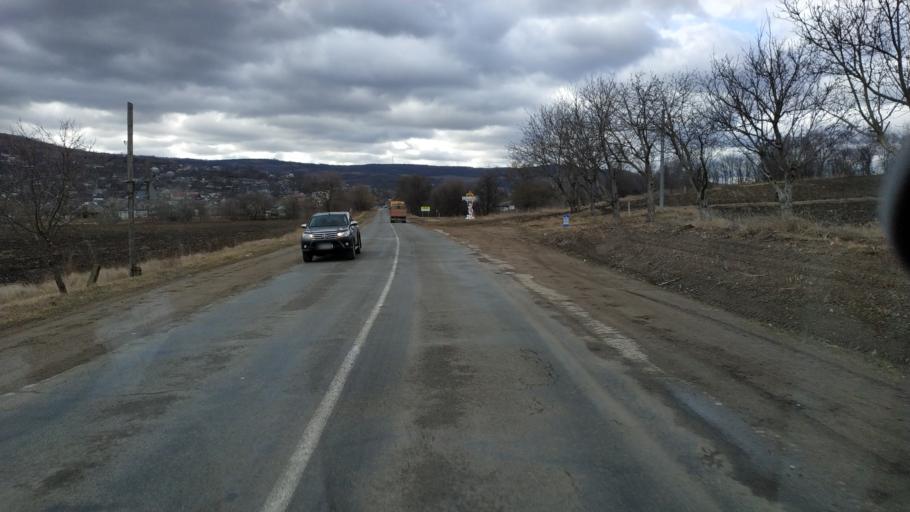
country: MD
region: Stinga Nistrului
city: Bucovat
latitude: 47.1653
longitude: 28.4364
